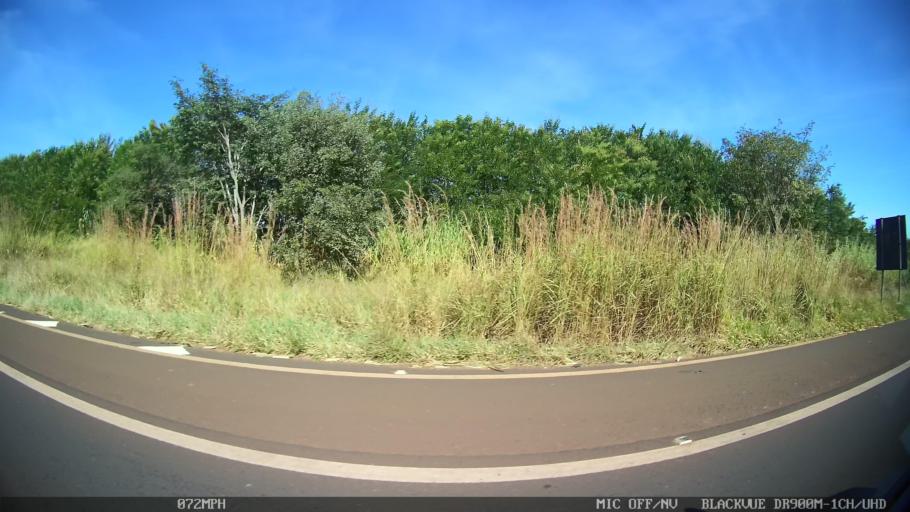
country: BR
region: Sao Paulo
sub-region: Franca
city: Franca
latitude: -20.5593
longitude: -47.5389
